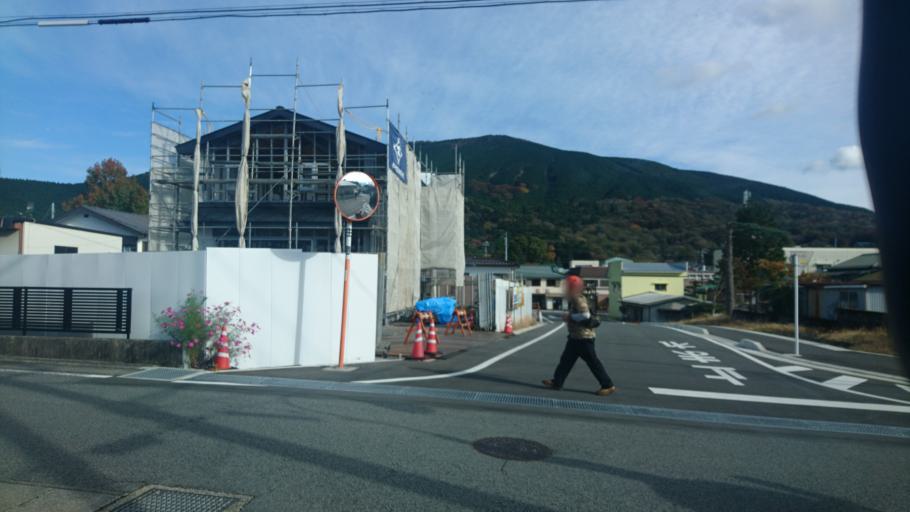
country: JP
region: Shizuoka
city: Gotemba
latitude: 35.3613
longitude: 138.8671
